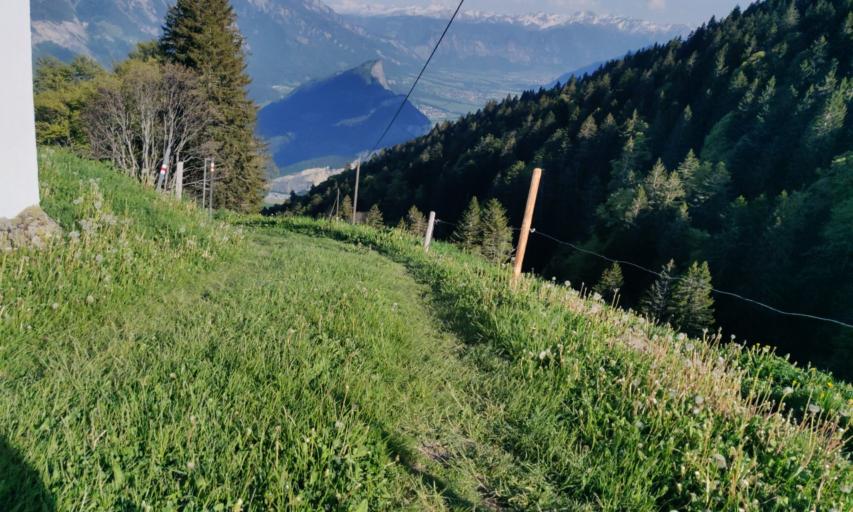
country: CH
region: Saint Gallen
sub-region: Wahlkreis Sarganserland
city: Sargans
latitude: 47.0762
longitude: 9.4389
